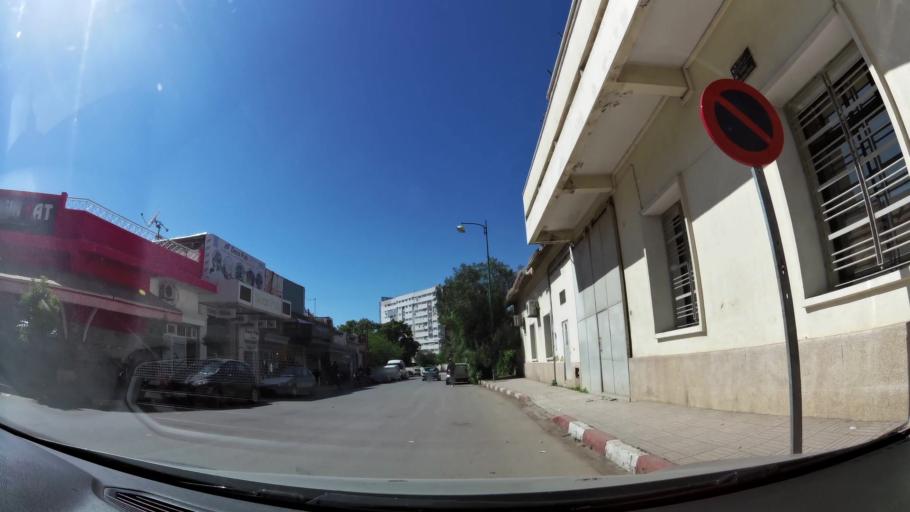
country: MA
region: Meknes-Tafilalet
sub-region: Meknes
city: Meknes
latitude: 33.8950
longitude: -5.5390
